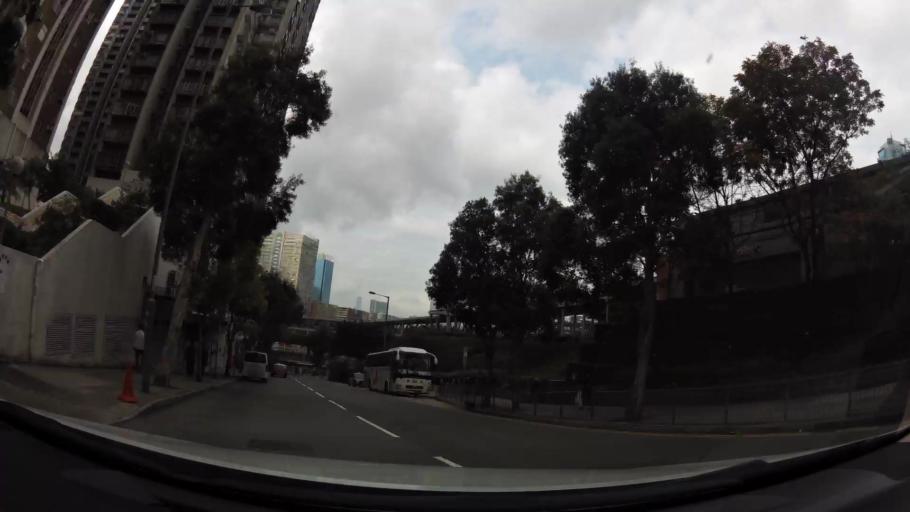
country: HK
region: Kowloon City
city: Kowloon
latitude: 22.3278
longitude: 114.2147
